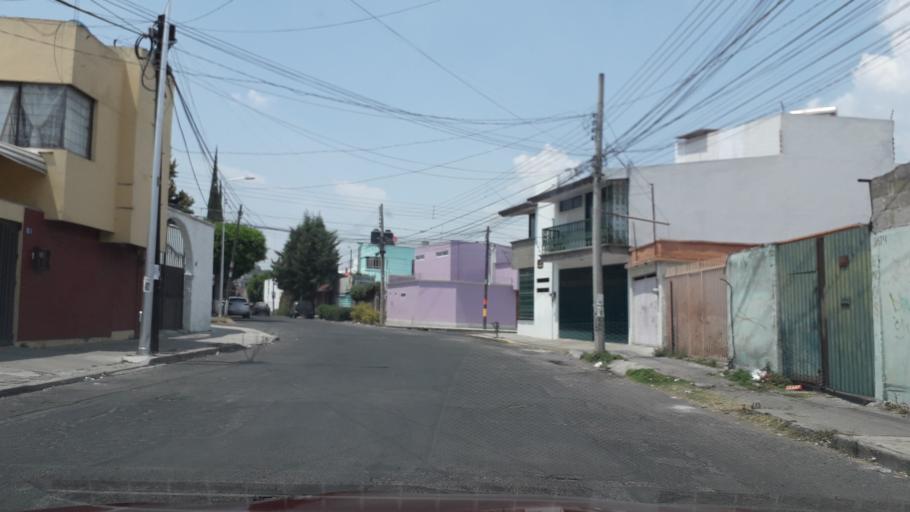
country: MX
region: Puebla
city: Puebla
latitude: 19.0456
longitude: -98.1726
